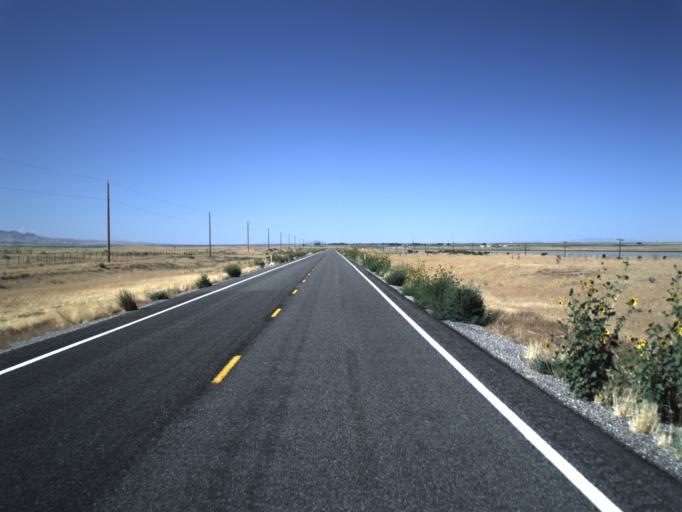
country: US
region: Utah
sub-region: Millard County
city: Delta
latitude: 39.6018
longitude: -112.3244
